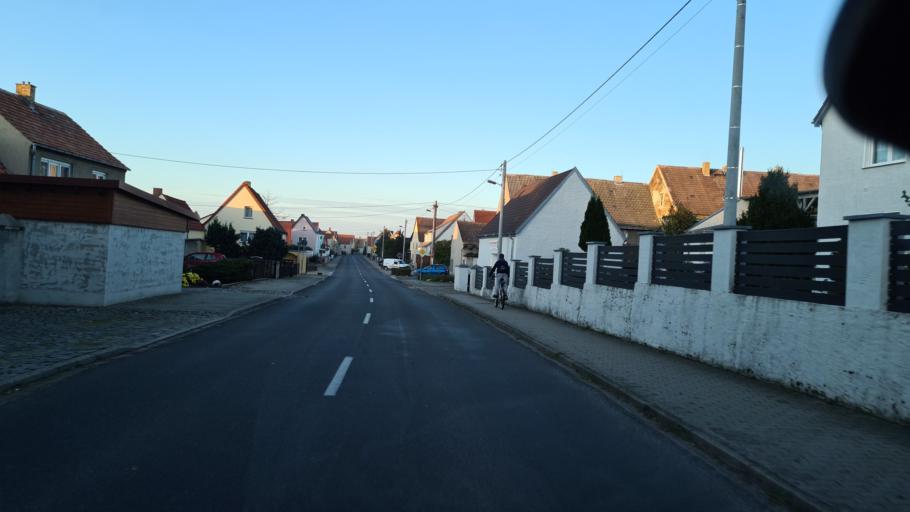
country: DE
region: Saxony
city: Schildau
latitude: 51.4474
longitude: 12.9705
